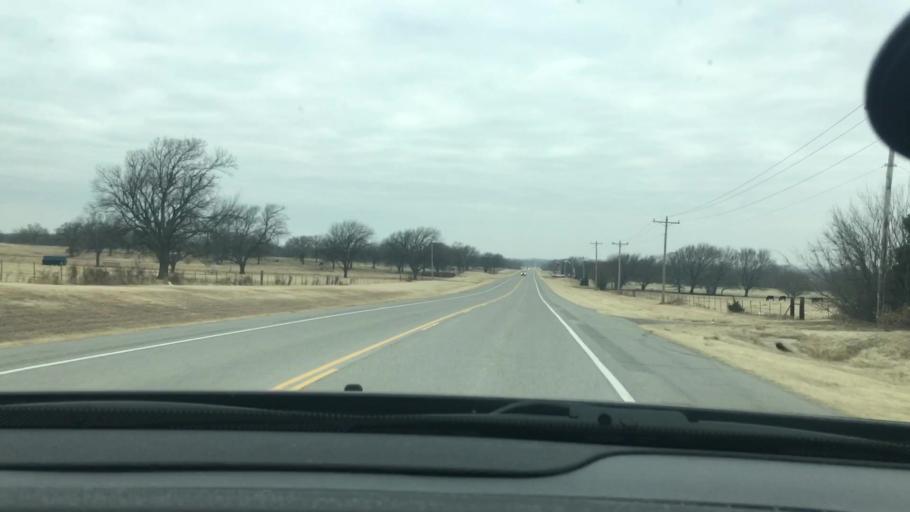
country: US
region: Oklahoma
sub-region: Carter County
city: Healdton
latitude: 34.4924
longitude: -97.4157
